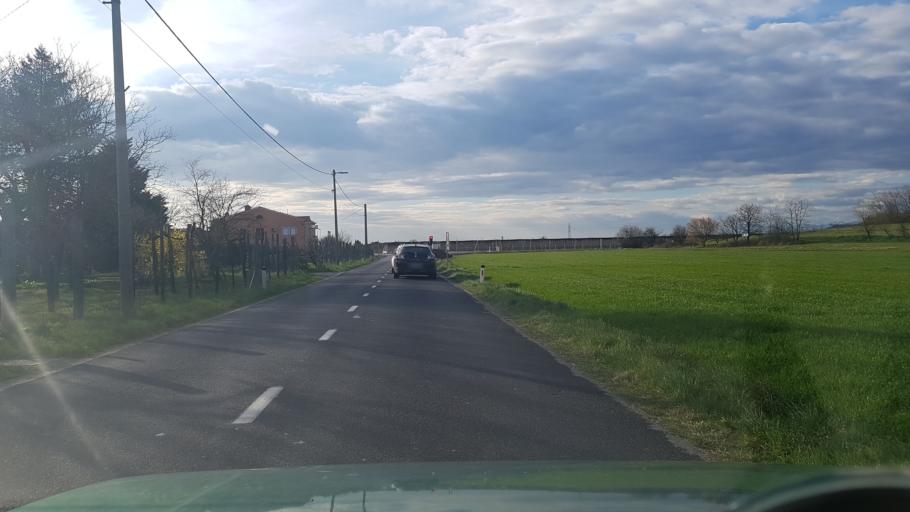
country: SI
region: Miren-Kostanjevica
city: Bilje
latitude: 45.8960
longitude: 13.6266
